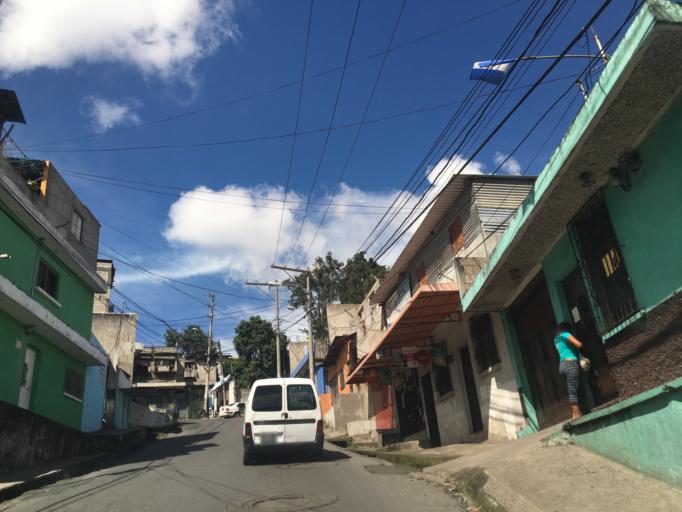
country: GT
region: Guatemala
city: Mixco
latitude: 14.6264
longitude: -90.5823
